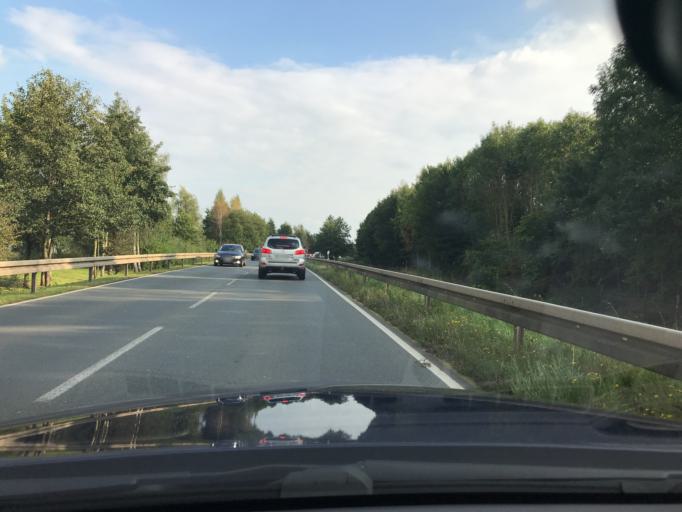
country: DE
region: Bremen
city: Bremen
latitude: 53.0156
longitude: 8.8705
